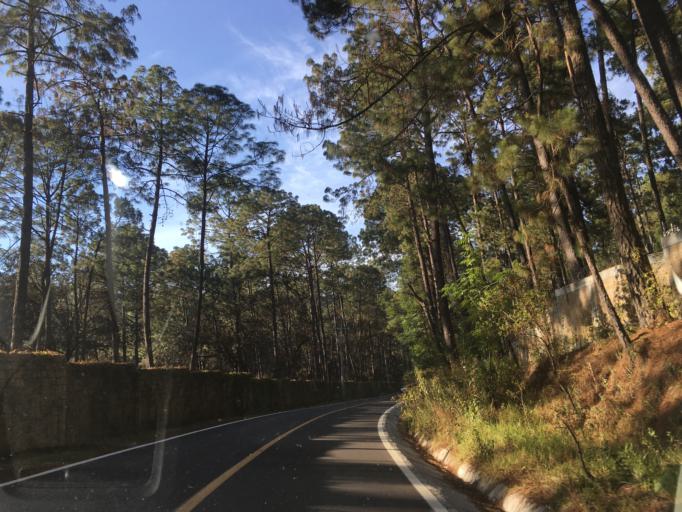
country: MX
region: Mexico
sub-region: Valle de Bravo
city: Casas Viejas
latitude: 19.1506
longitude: -100.1255
